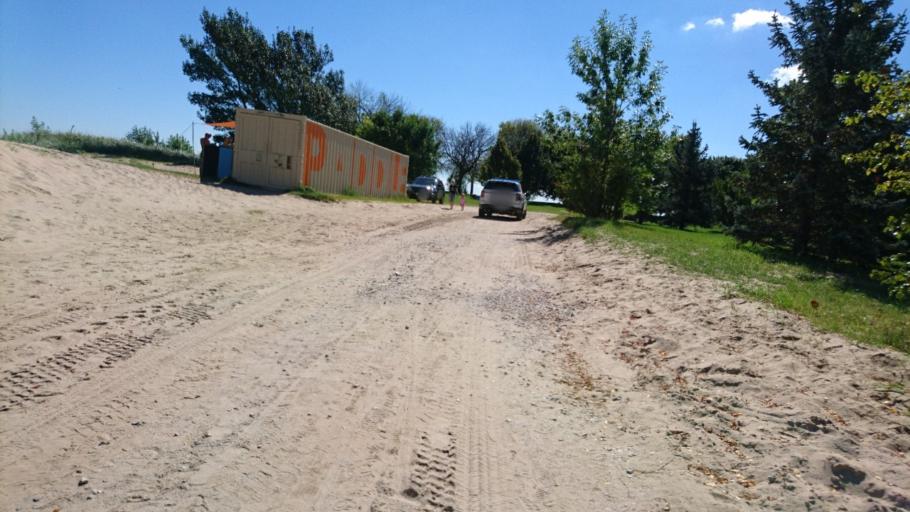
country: US
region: Illinois
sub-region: Cook County
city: Evanston
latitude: 41.9853
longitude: -87.6515
